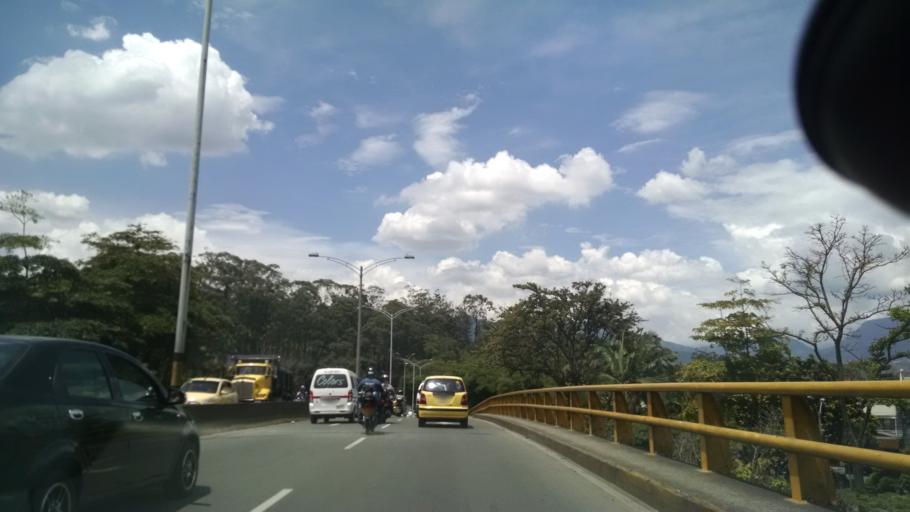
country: CO
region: Antioquia
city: Itagui
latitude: 6.2043
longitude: -75.5870
